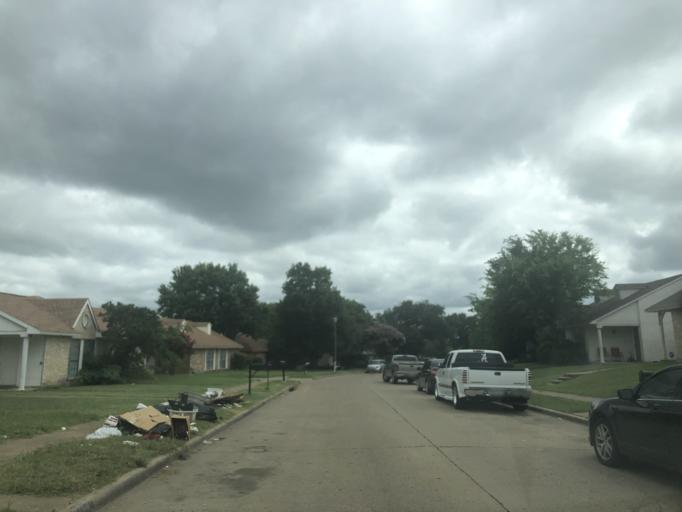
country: US
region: Texas
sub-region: Dallas County
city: Duncanville
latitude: 32.6357
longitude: -96.9470
